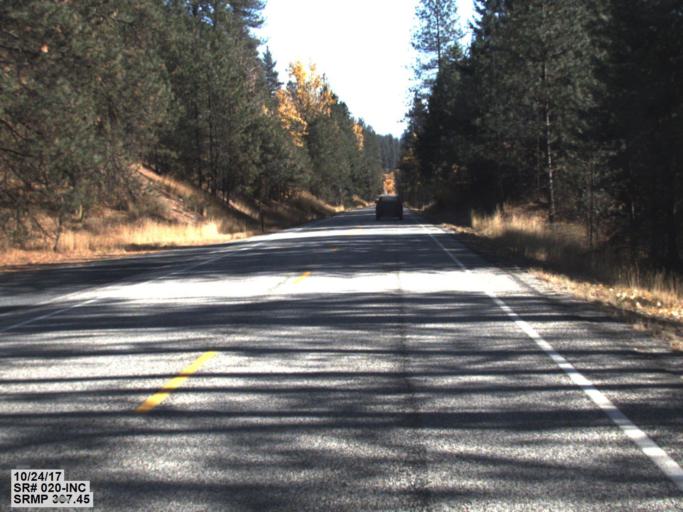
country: US
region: Washington
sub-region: Stevens County
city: Kettle Falls
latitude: 48.5922
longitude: -118.1793
